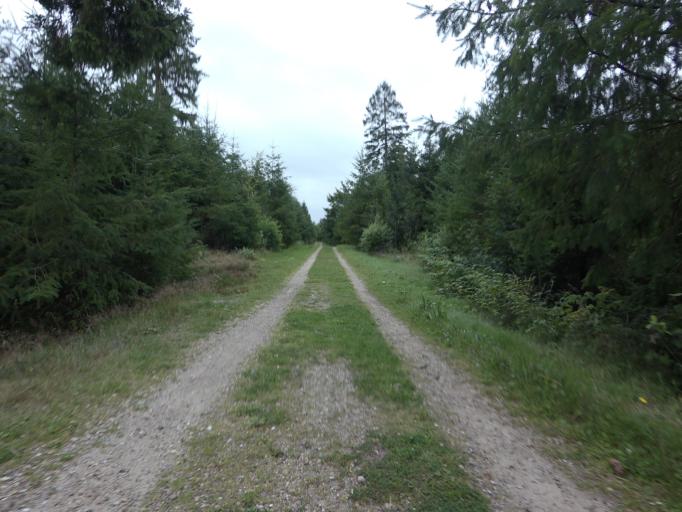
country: DK
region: Central Jutland
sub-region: Silkeborg Kommune
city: Virklund
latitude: 56.0373
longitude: 9.4701
